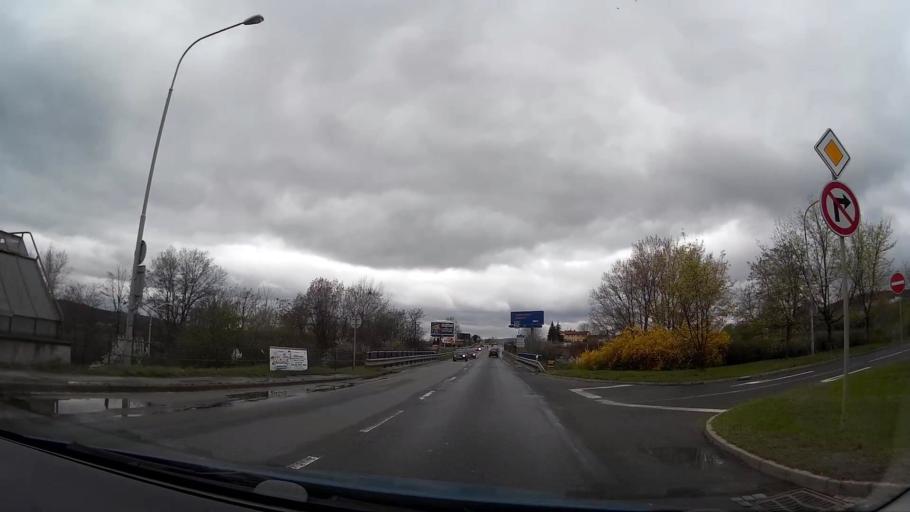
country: CZ
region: South Moravian
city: Ostopovice
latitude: 49.1734
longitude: 16.5530
